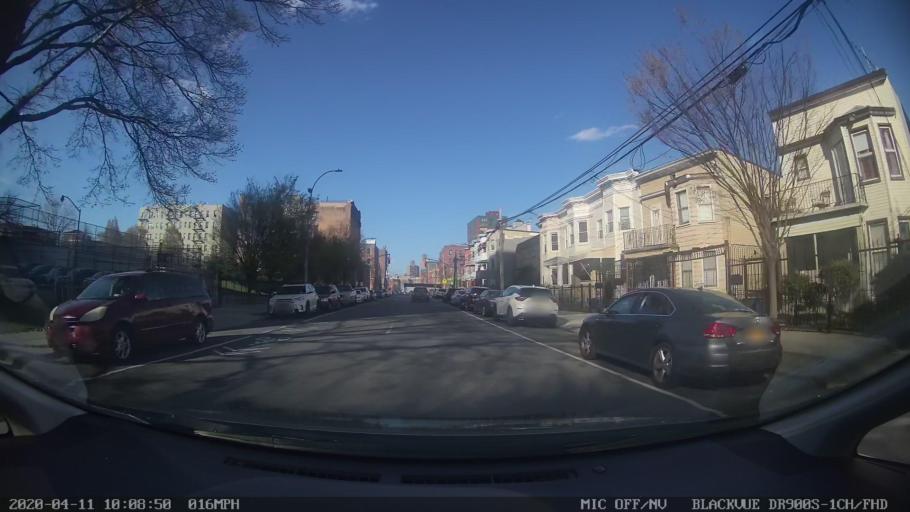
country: US
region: New York
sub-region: Bronx
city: The Bronx
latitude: 40.8494
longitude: -73.8875
